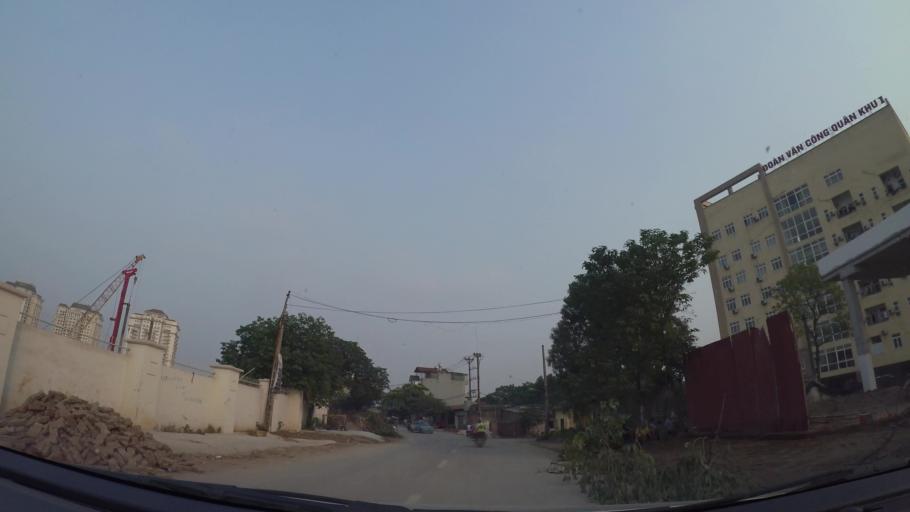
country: VN
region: Ha Noi
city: Tay Ho
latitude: 21.0786
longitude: 105.7883
